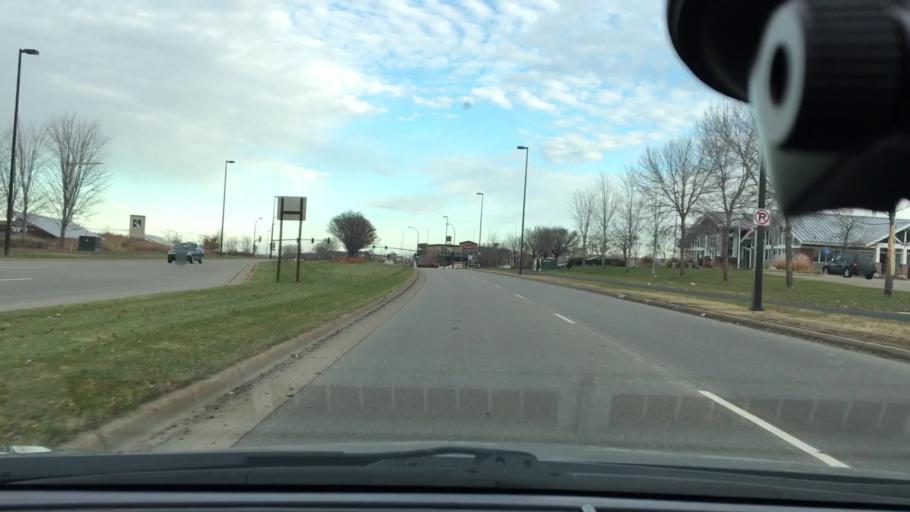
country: US
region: Minnesota
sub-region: Hennepin County
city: Maple Grove
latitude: 45.0942
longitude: -93.4402
